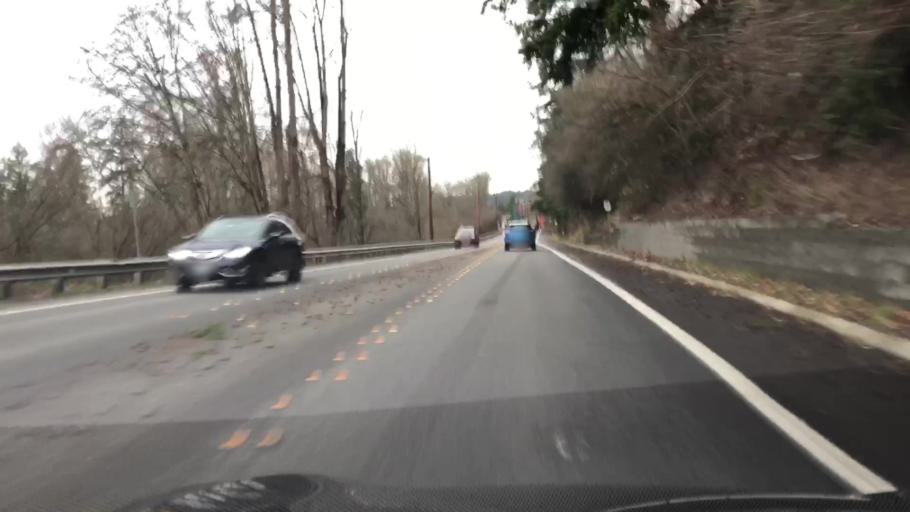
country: US
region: Washington
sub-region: King County
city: Sammamish
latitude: 47.6569
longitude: -122.0940
